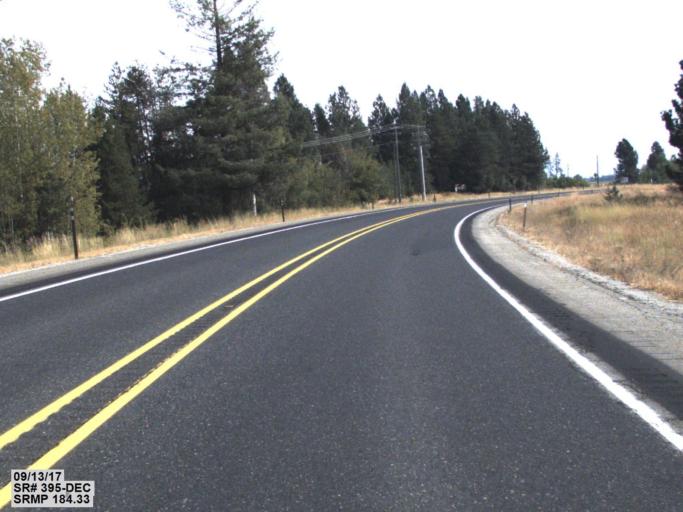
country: US
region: Washington
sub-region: Spokane County
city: Deer Park
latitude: 47.9935
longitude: -117.5470
